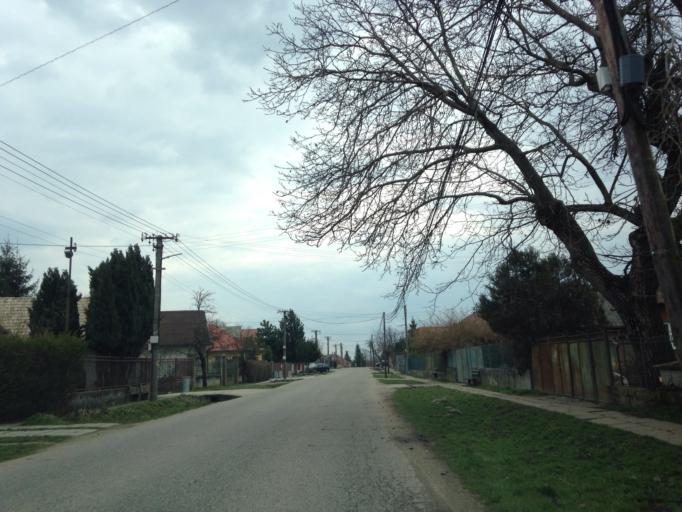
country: SK
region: Nitriansky
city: Svodin
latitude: 47.9242
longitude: 18.4032
